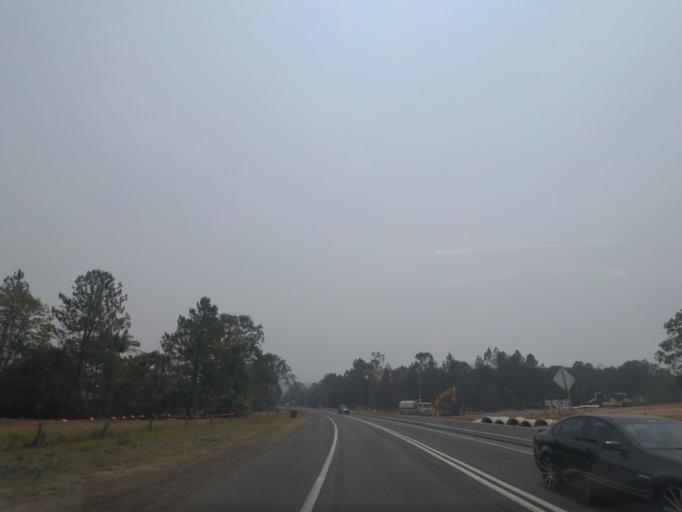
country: AU
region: New South Wales
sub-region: Clarence Valley
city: Maclean
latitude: -29.5497
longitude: 153.1557
